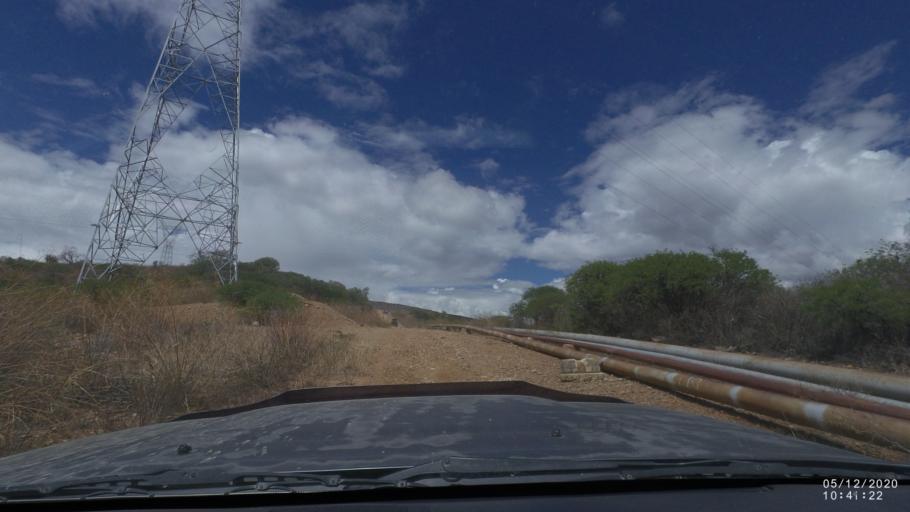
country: BO
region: Cochabamba
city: Sipe Sipe
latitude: -17.5459
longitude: -66.2912
